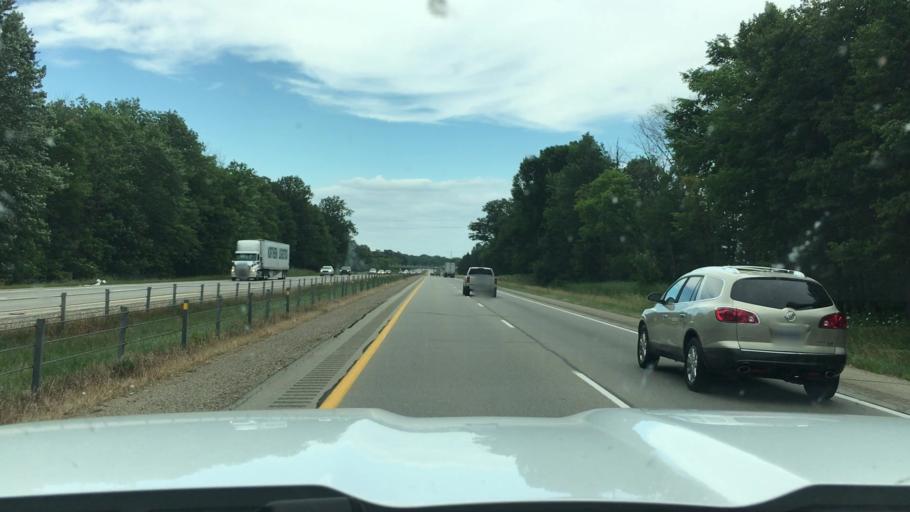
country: US
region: Michigan
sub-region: Allegan County
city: Wayland
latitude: 42.7478
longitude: -85.6734
